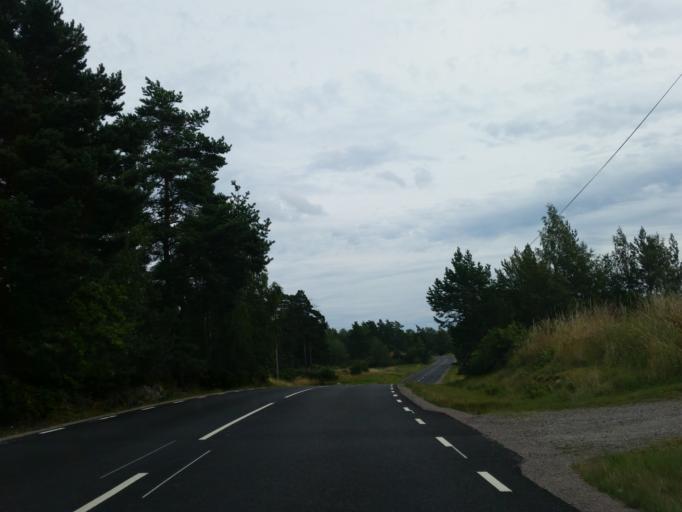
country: SE
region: Soedermanland
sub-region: Strangnas Kommun
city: Akers Styckebruk
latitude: 59.2728
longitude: 17.1439
